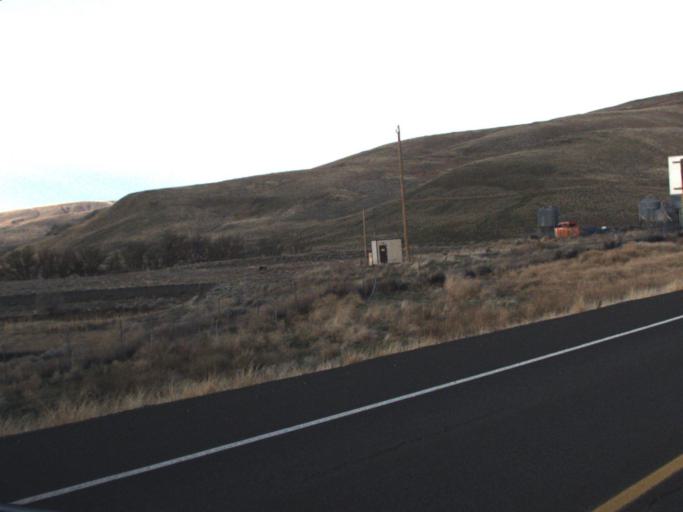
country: US
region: Washington
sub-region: Garfield County
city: Pomeroy
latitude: 46.6336
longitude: -117.8076
